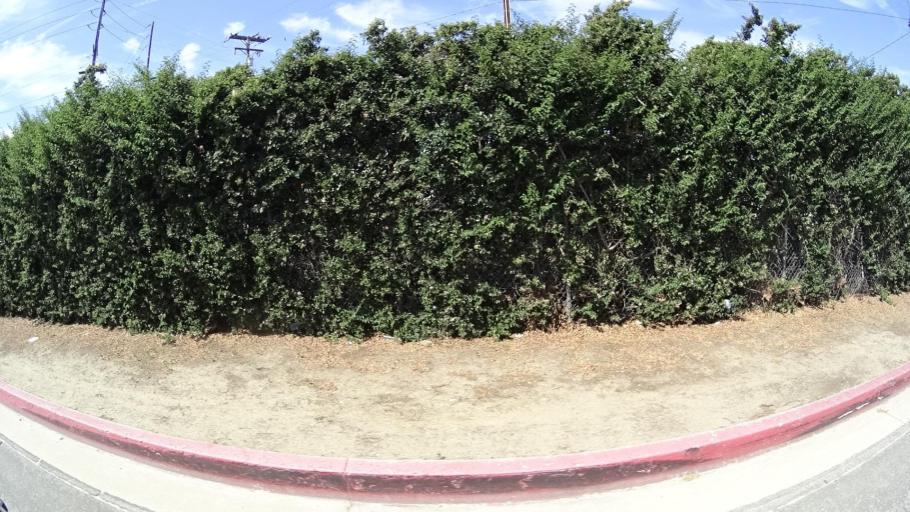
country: US
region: California
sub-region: Los Angeles County
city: South San Jose Hills
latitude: 33.9998
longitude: -117.9235
